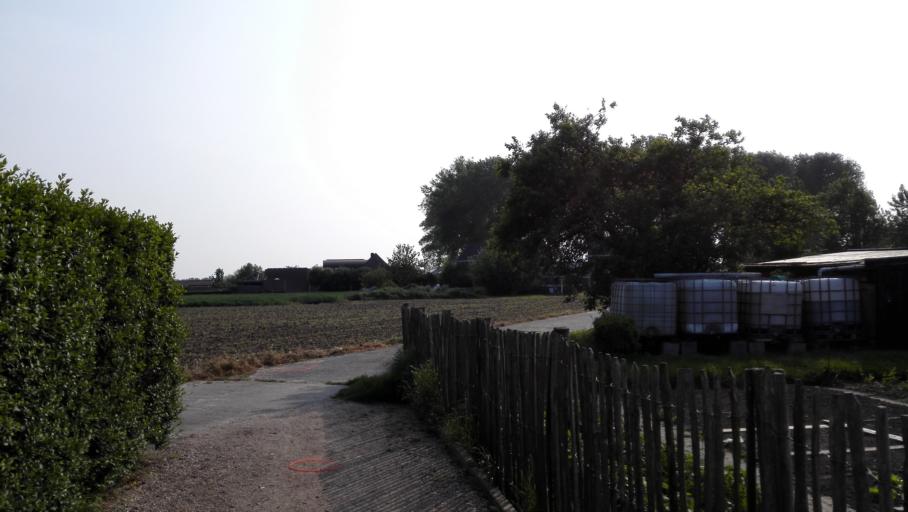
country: BE
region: Flanders
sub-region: Provincie West-Vlaanderen
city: Zeebrugge
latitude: 51.3094
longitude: 3.2009
